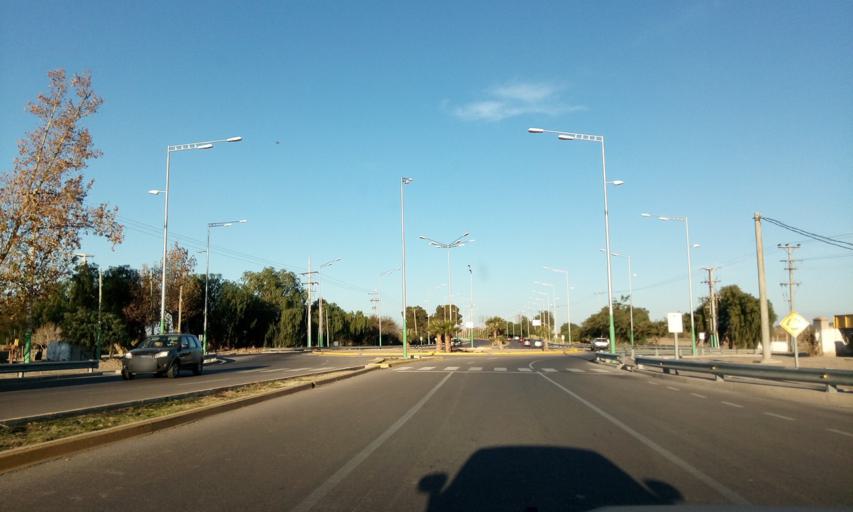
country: AR
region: San Juan
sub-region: Departamento de Rivadavia
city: Rivadavia
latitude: -31.5233
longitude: -68.6171
